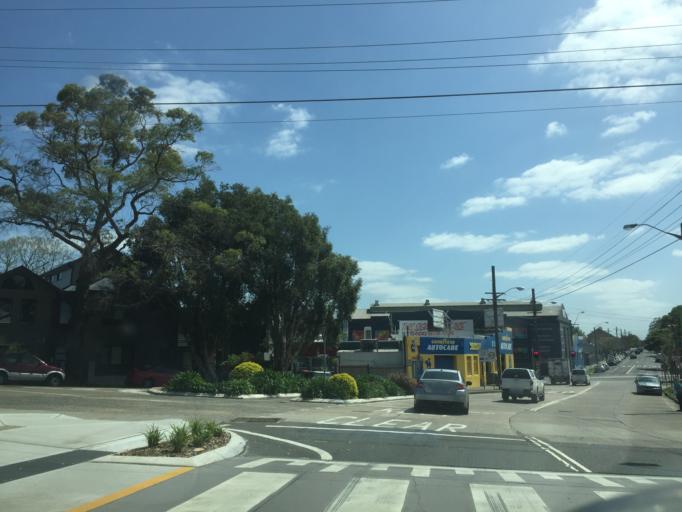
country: AU
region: New South Wales
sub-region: Marrickville
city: Lewisham
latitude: -33.8908
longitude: 151.1489
